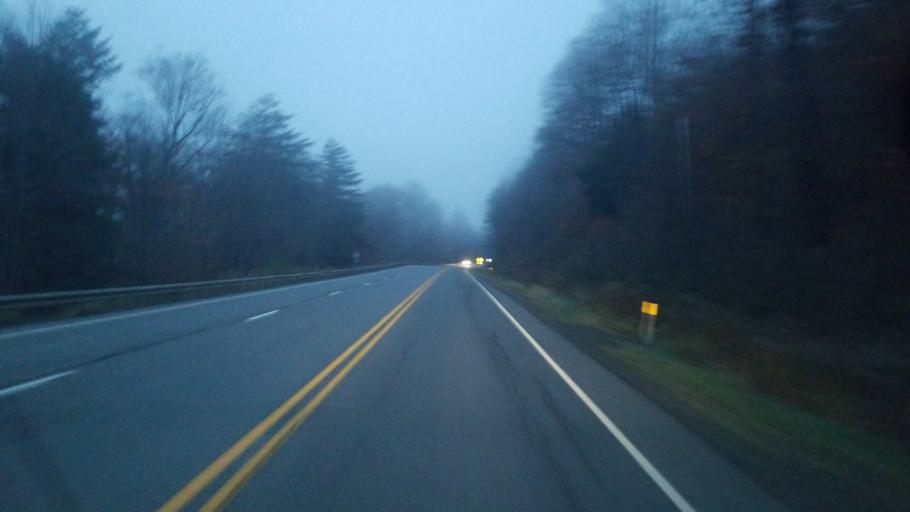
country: US
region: Pennsylvania
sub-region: McKean County
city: Smethport
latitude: 41.7223
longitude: -78.6144
